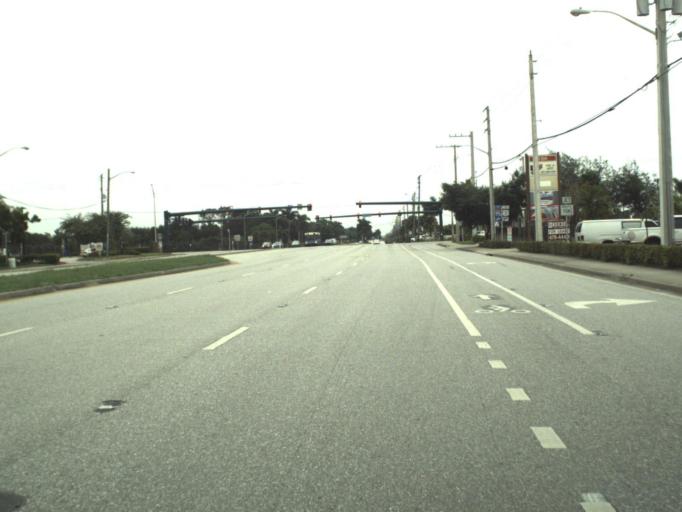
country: US
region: Florida
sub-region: Palm Beach County
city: Mangonia Park
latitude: 26.7819
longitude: -80.1072
